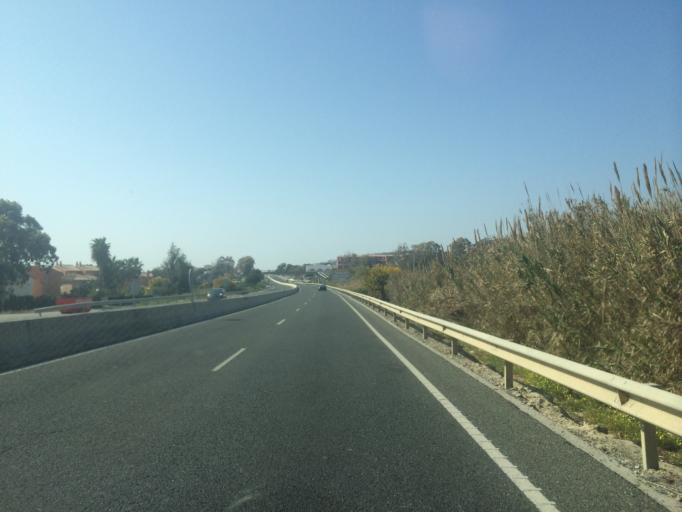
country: ES
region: Andalusia
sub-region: Provincia de Malaga
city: Manilva
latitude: 36.3468
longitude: -5.2367
